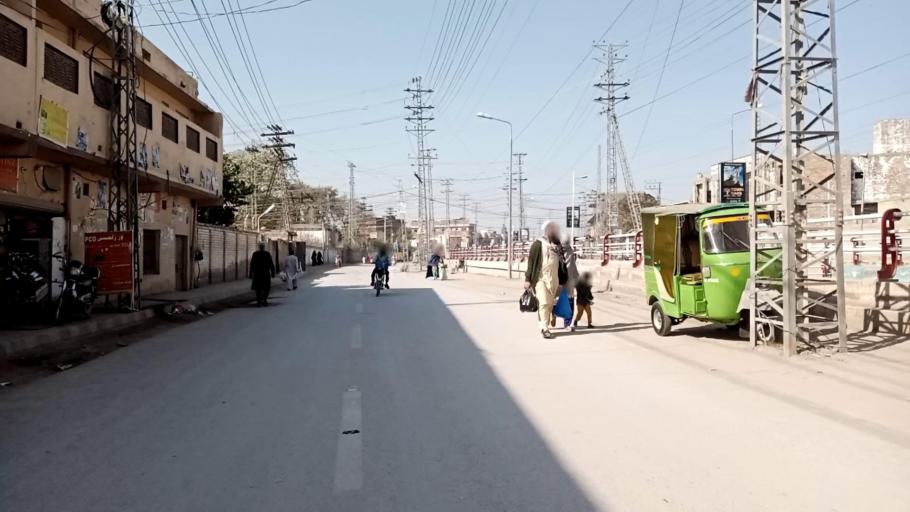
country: PK
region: Khyber Pakhtunkhwa
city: Peshawar
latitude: 33.9932
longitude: 71.4746
